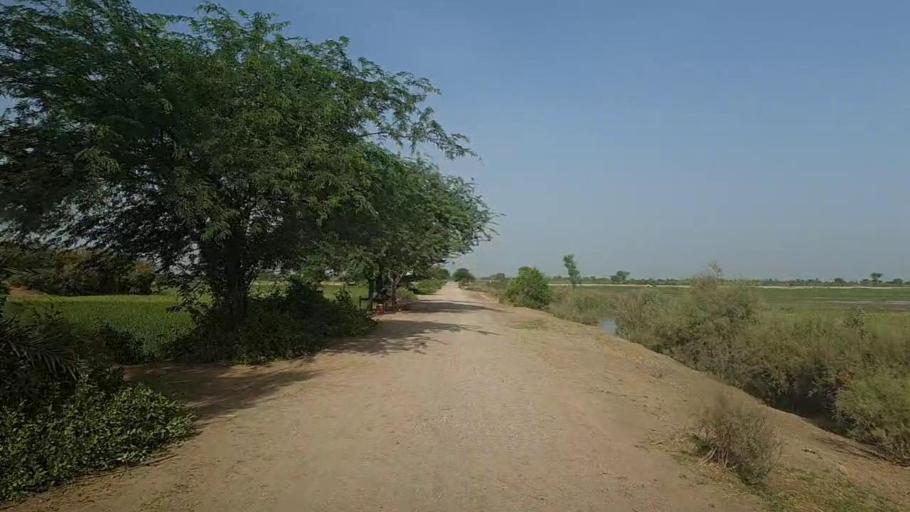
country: PK
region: Sindh
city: Sita Road
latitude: 27.0933
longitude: 67.8663
